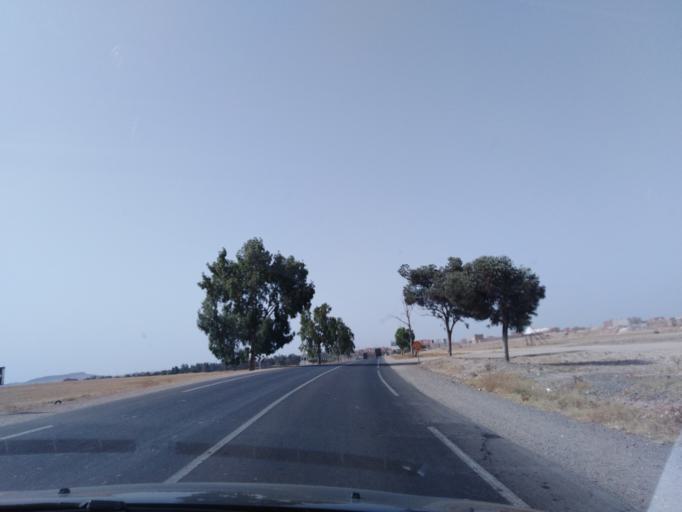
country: MA
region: Marrakech-Tensift-Al Haouz
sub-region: Kelaa-Des-Sraghna
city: Sidi Bou Othmane
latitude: 32.2200
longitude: -7.9570
